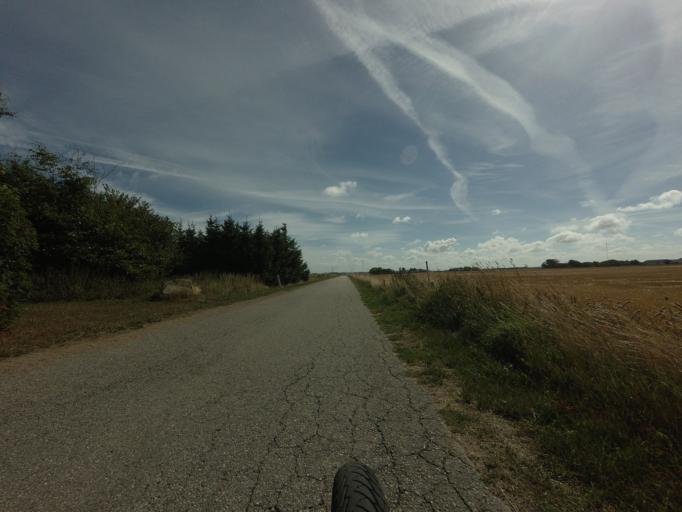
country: DK
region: North Denmark
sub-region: Hjorring Kommune
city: Vra
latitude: 57.3427
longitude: 9.7880
